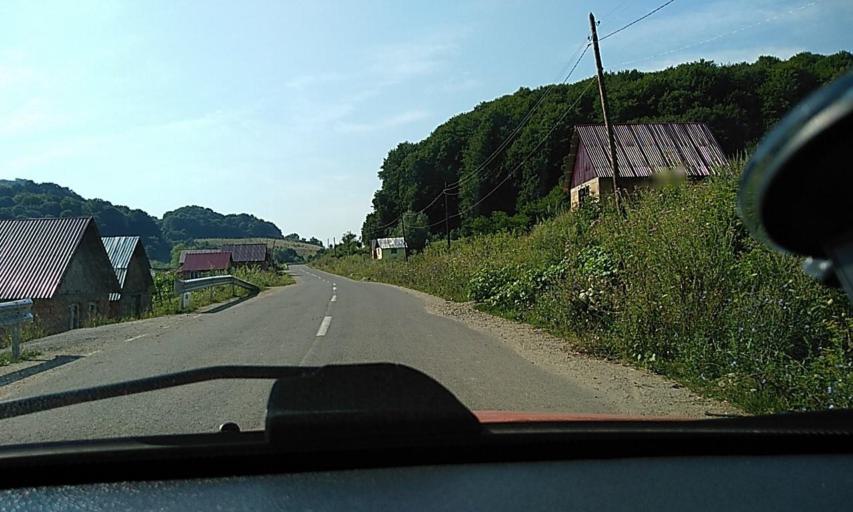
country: RO
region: Brasov
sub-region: Comuna Bunesti
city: Bunesti
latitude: 46.0981
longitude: 25.0569
